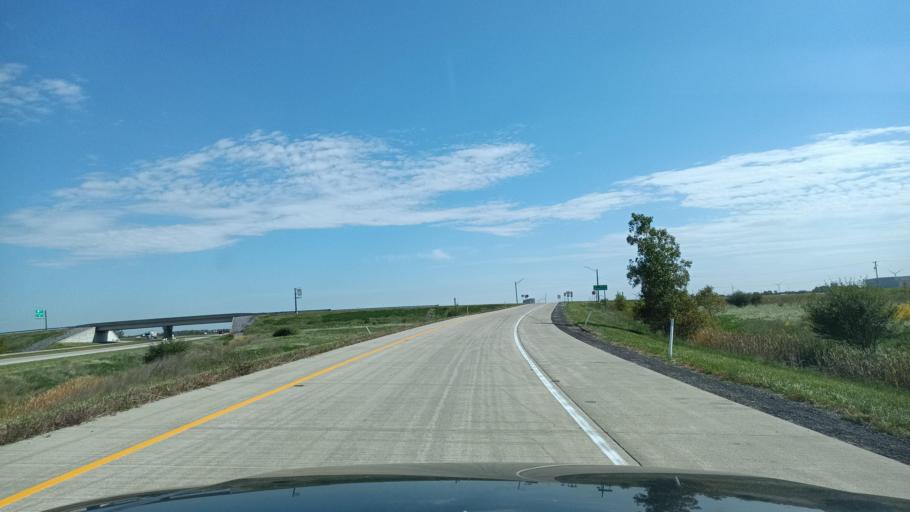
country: US
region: Indiana
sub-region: Allen County
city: Woodburn
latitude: 41.1430
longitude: -84.8516
